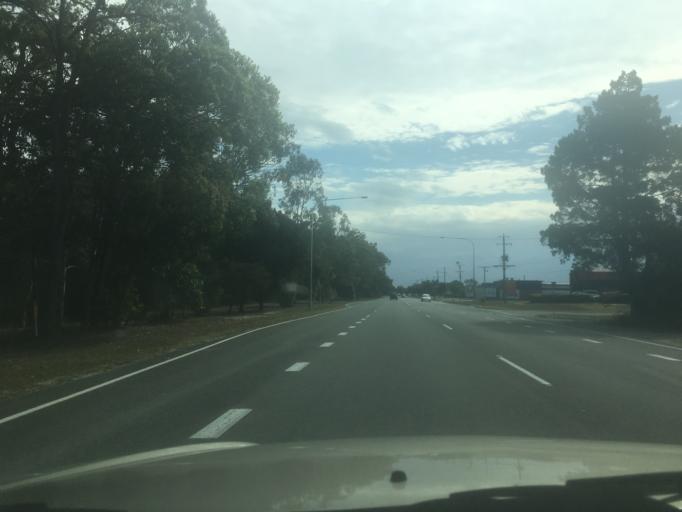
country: AU
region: Queensland
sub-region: Moreton Bay
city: Bongaree
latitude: -27.0779
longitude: 153.1817
